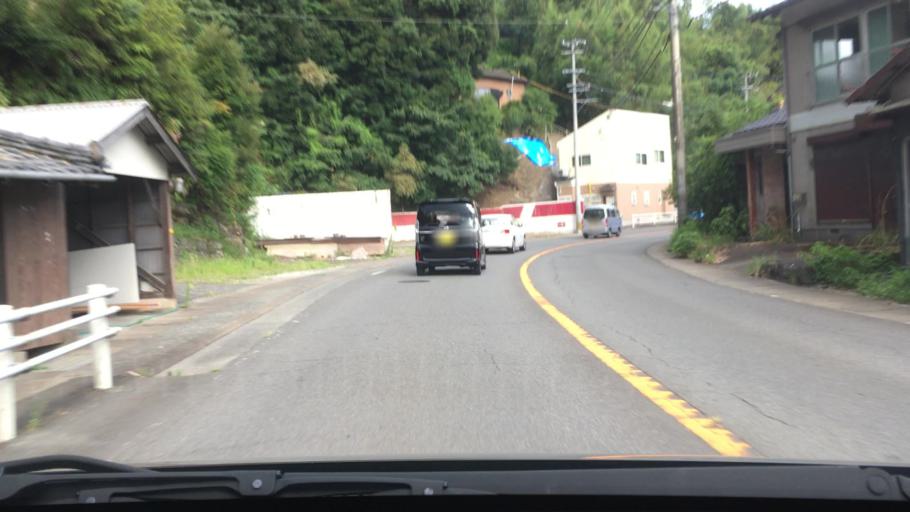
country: JP
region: Nagasaki
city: Togitsu
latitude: 32.8256
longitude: 129.7864
